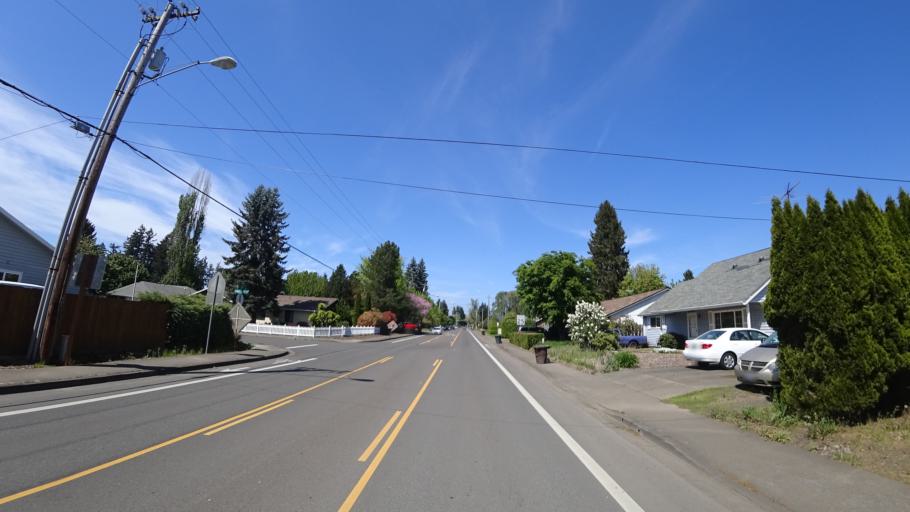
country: US
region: Oregon
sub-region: Washington County
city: Hillsboro
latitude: 45.5166
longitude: -122.9497
